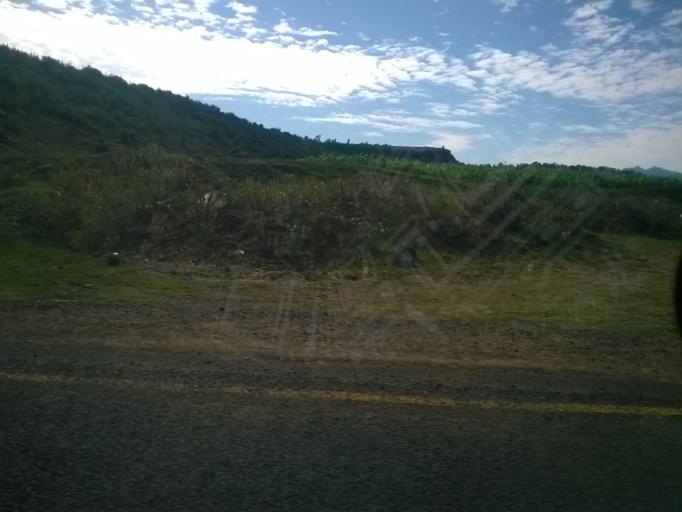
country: LS
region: Berea
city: Teyateyaneng
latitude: -29.0907
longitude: 27.9441
